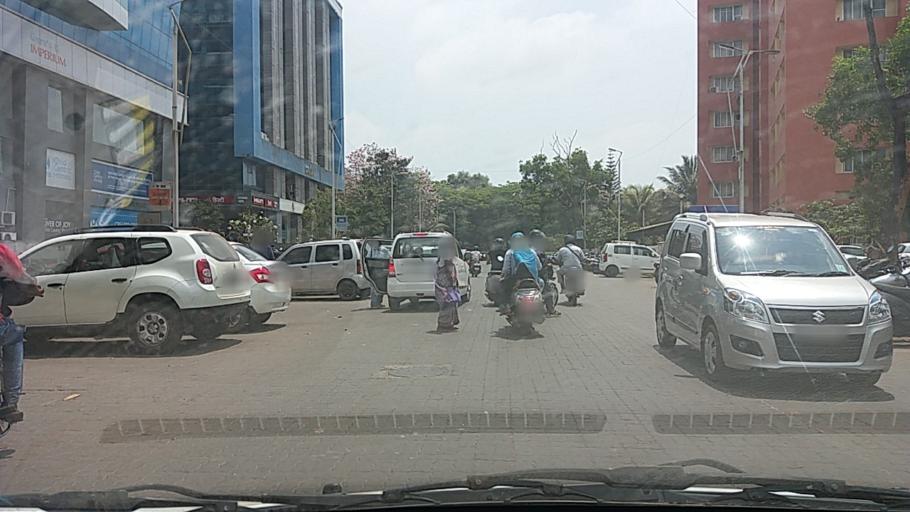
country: IN
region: Goa
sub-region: North Goa
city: Panaji
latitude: 15.4937
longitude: 73.8356
